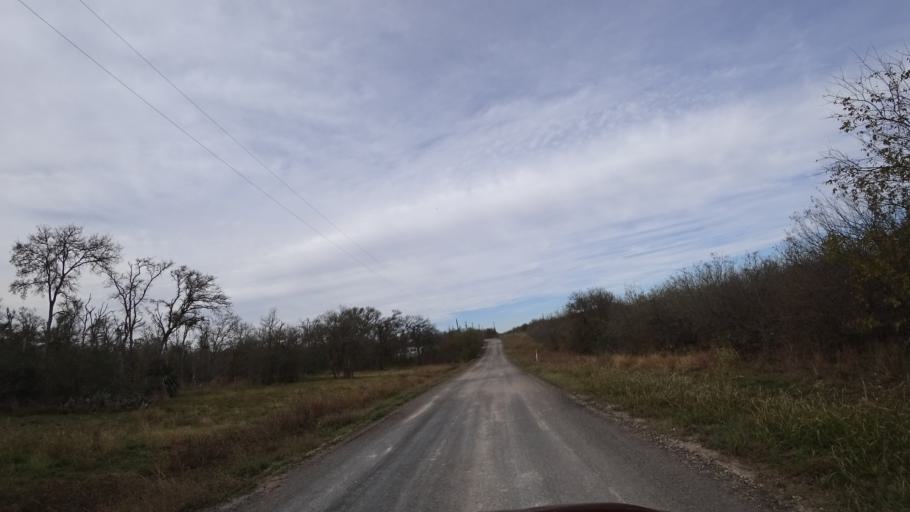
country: US
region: Texas
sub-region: Travis County
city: Garfield
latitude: 30.1082
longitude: -97.5717
